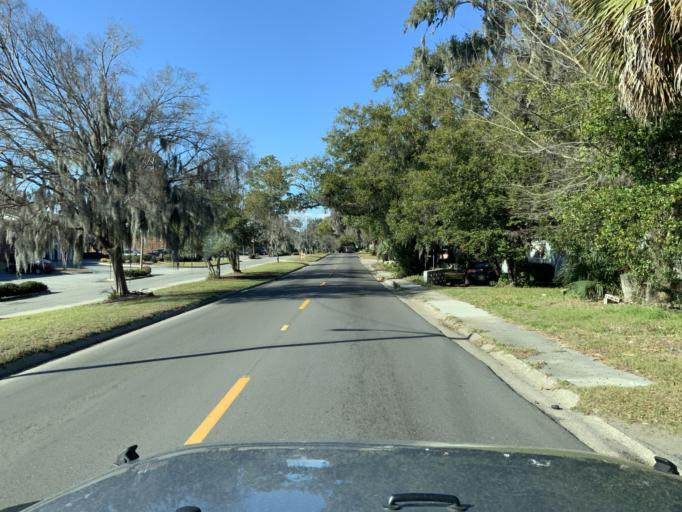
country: US
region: Georgia
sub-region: Chatham County
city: Thunderbolt
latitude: 32.0508
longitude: -81.0658
